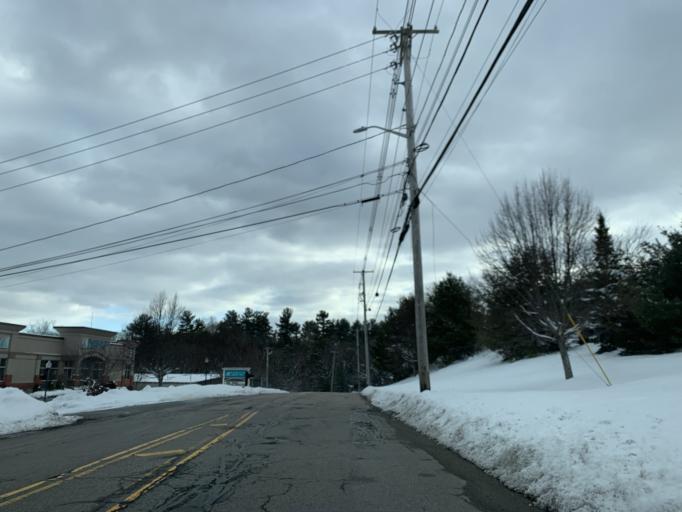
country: US
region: Massachusetts
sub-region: Norfolk County
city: Franklin
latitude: 42.0696
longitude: -71.4249
